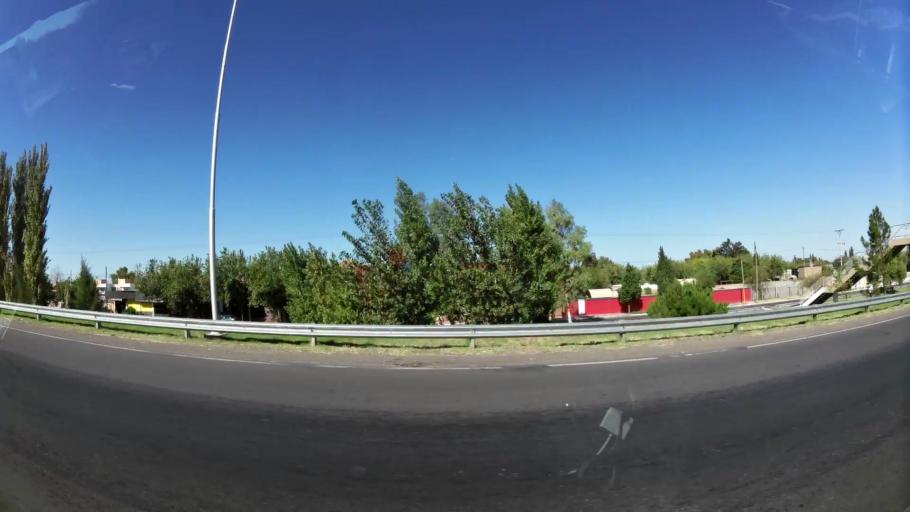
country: AR
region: San Juan
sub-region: Departamento de Santa Lucia
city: Santa Lucia
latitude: -31.5379
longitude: -68.5038
